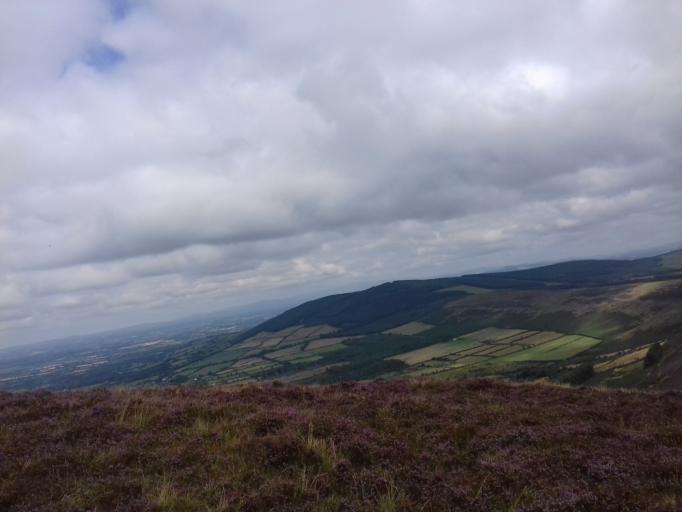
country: IE
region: Leinster
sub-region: Loch Garman
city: Bunclody
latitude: 52.6378
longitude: -6.7971
